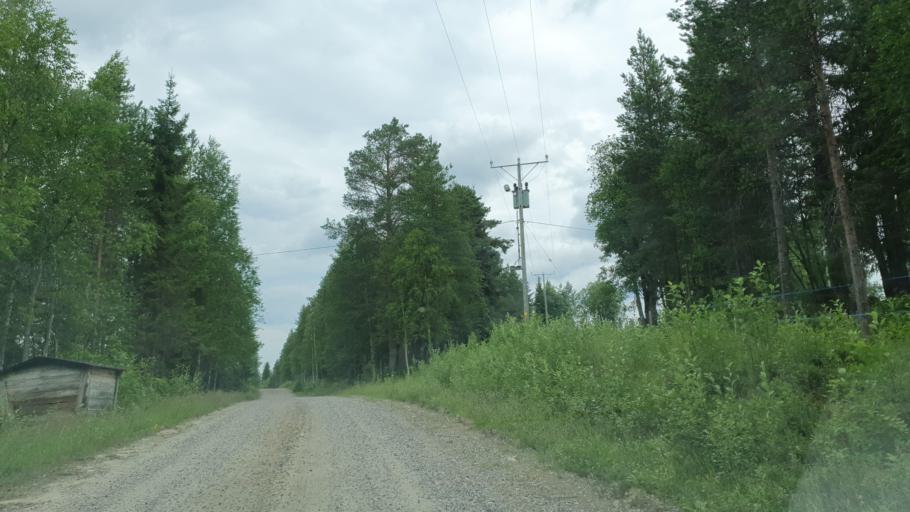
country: FI
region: Kainuu
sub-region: Kehys-Kainuu
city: Kuhmo
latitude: 64.7317
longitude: 29.6369
